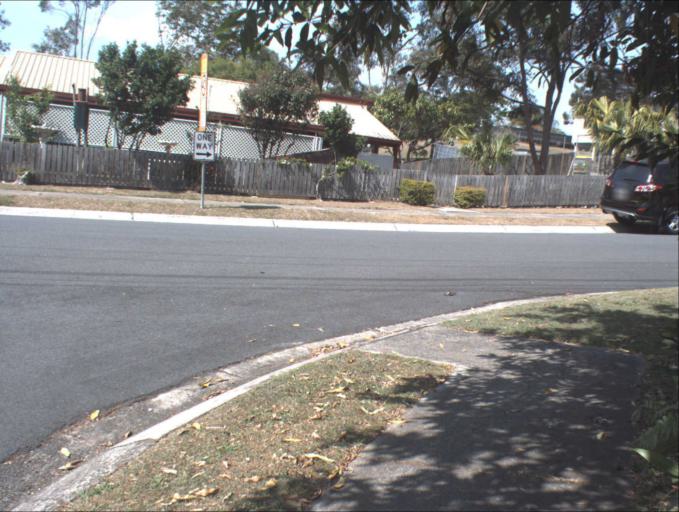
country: AU
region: Queensland
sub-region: Logan
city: Slacks Creek
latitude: -27.6594
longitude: 153.1888
